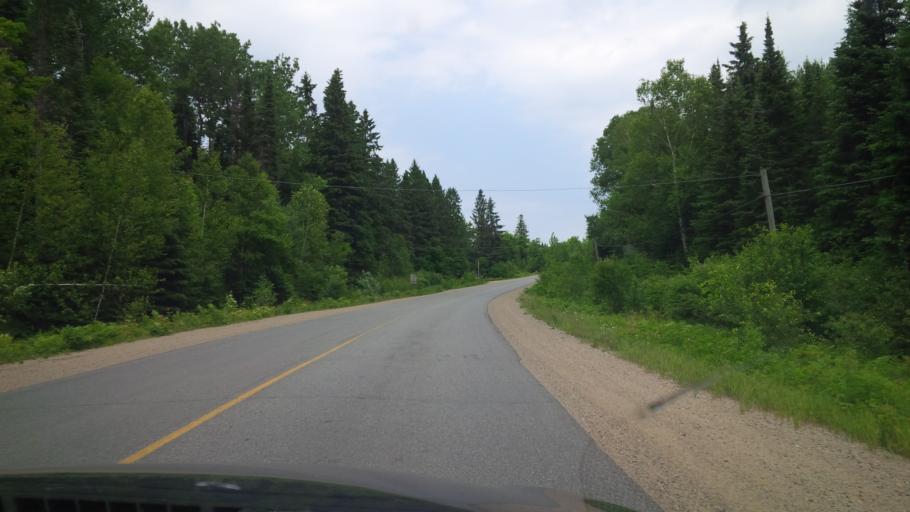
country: CA
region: Ontario
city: Huntsville
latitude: 45.6065
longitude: -79.1765
